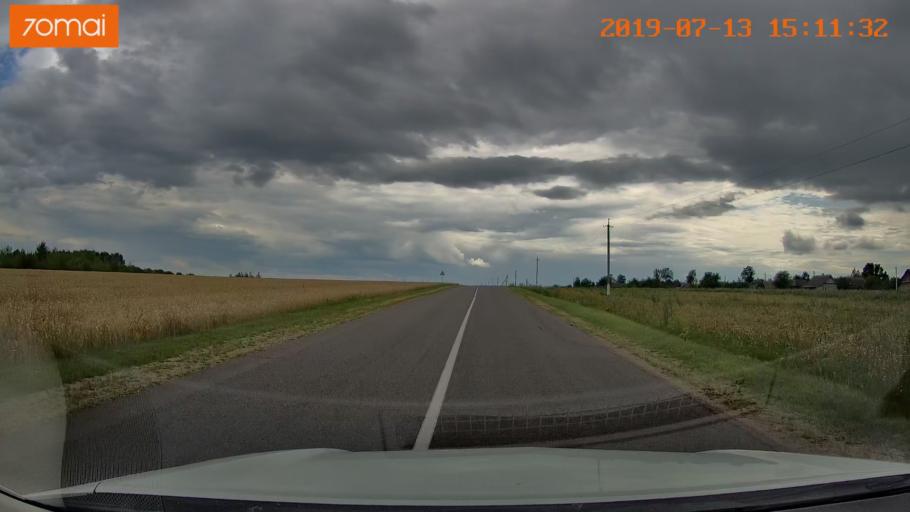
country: BY
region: Mogilev
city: Hlusha
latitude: 53.1600
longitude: 28.7866
